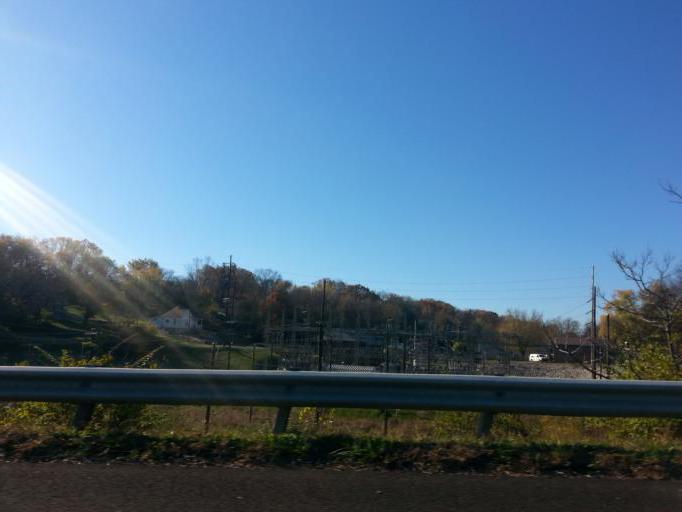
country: US
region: Tennessee
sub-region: Knox County
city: Knoxville
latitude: 35.9839
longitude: -83.9468
